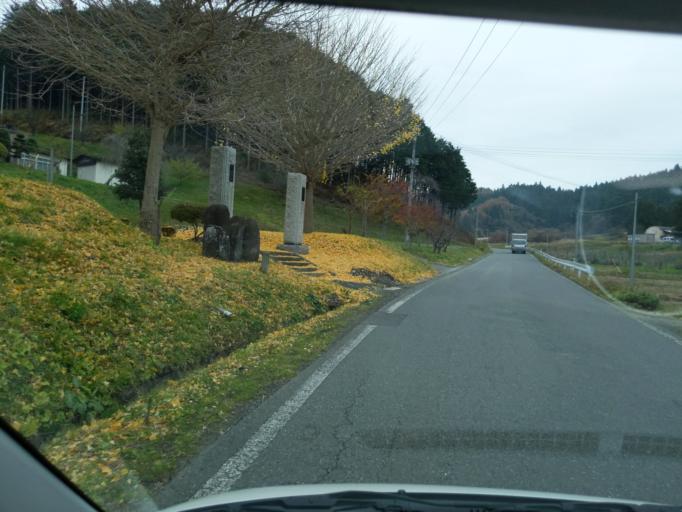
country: JP
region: Iwate
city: Kitakami
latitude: 39.2811
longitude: 141.1755
